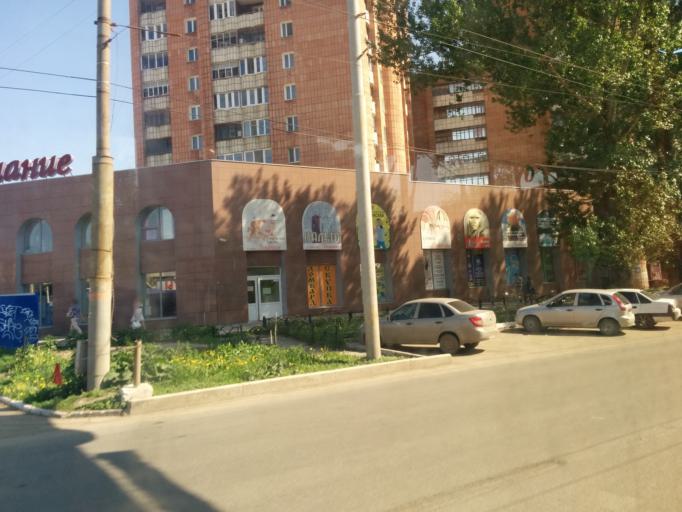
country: RU
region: Perm
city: Perm
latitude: 58.0140
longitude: 56.2810
